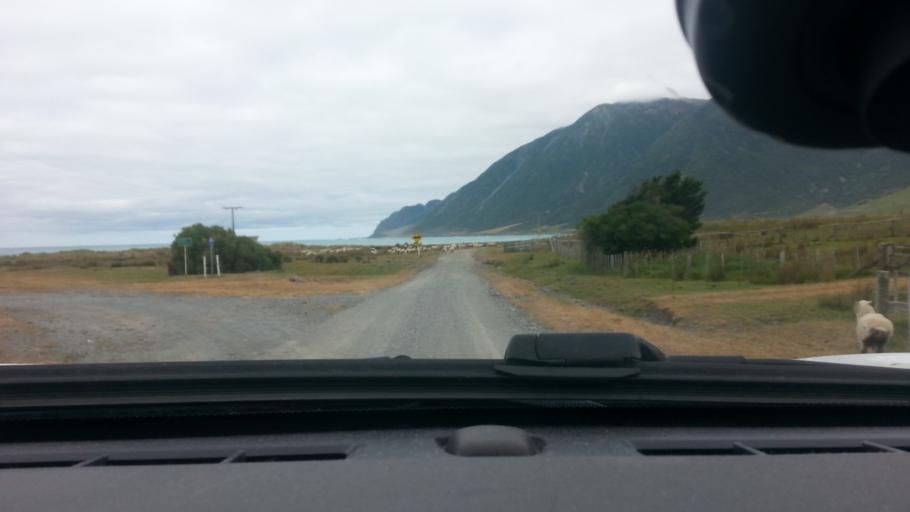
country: NZ
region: Wellington
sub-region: South Wairarapa District
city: Waipawa
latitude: -41.5667
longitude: 175.3960
